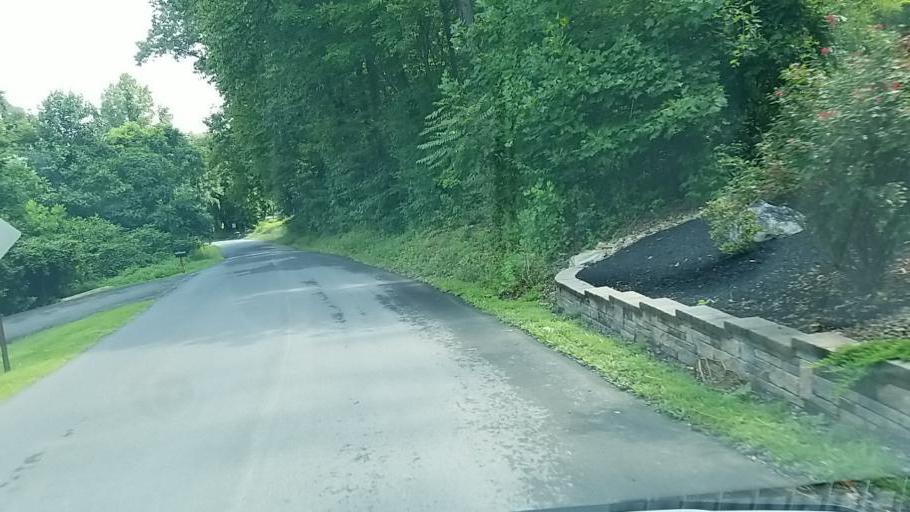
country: US
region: Pennsylvania
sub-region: Dauphin County
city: Millersburg
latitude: 40.5276
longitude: -76.9614
